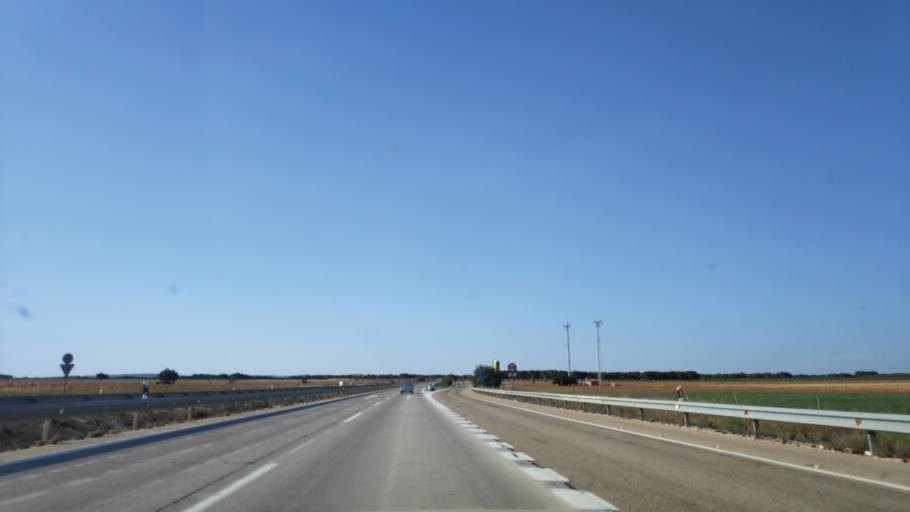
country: ES
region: Castille-La Mancha
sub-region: Provincia de Cuenca
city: Pozoamargo
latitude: 39.3190
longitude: -2.2034
